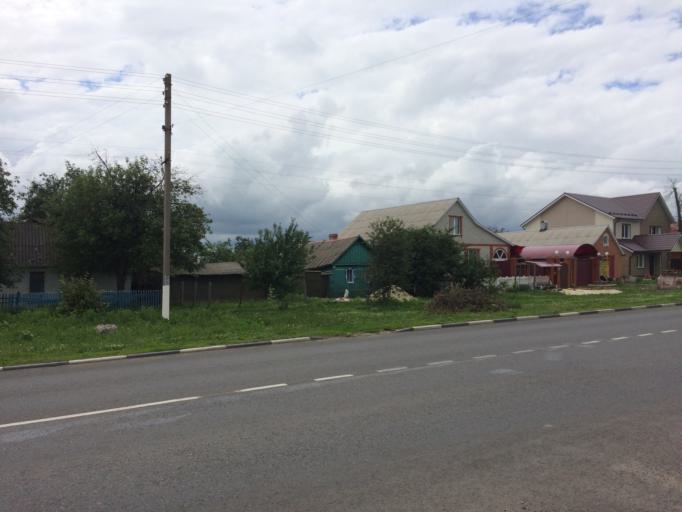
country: RU
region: Kursk
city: Zolotukhino
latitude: 51.9685
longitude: 36.3032
